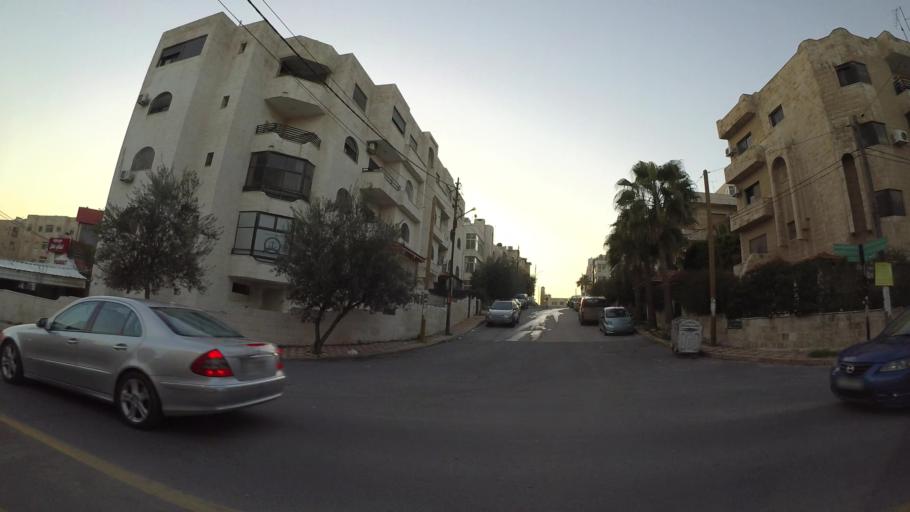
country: JO
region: Amman
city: Al Jubayhah
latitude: 31.9883
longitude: 35.8848
